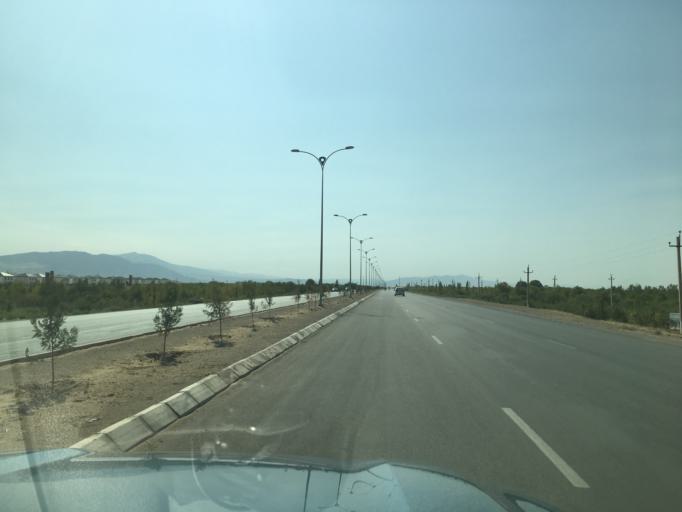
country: TM
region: Ahal
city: Abadan
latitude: 38.1028
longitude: 58.3033
